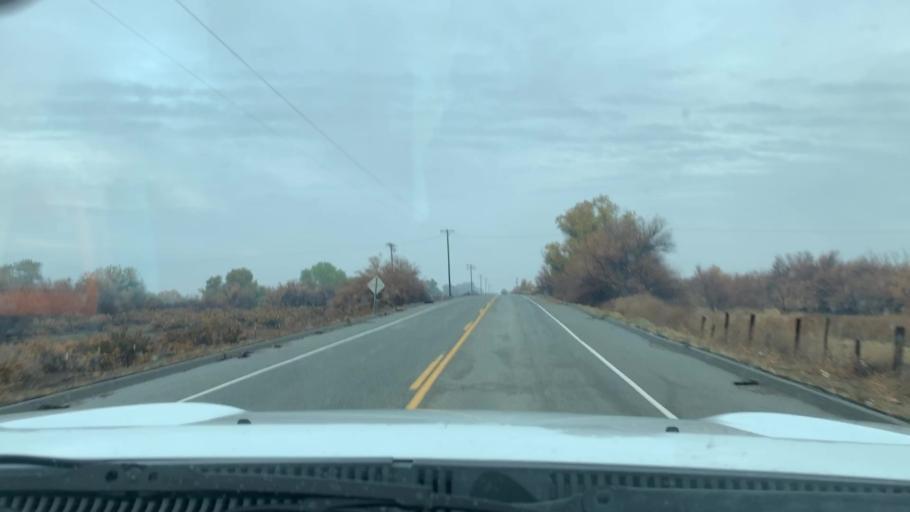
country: US
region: California
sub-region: Kern County
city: Lost Hills
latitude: 35.7163
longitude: -119.5795
